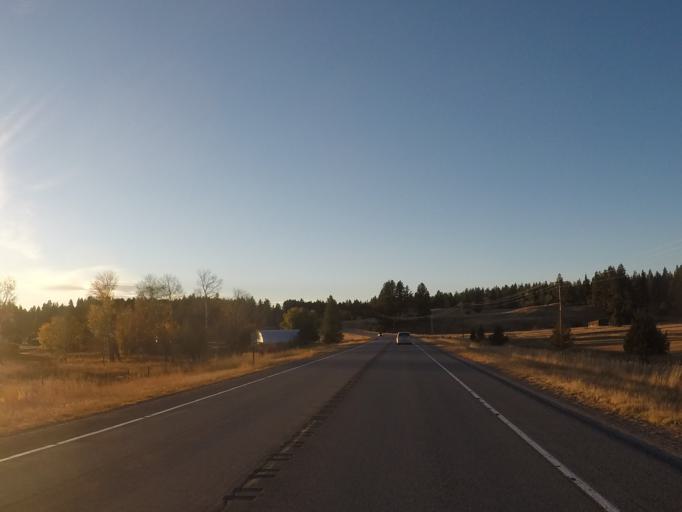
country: US
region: Montana
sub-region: Lewis and Clark County
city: Lincoln
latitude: 47.0058
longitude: -113.0472
